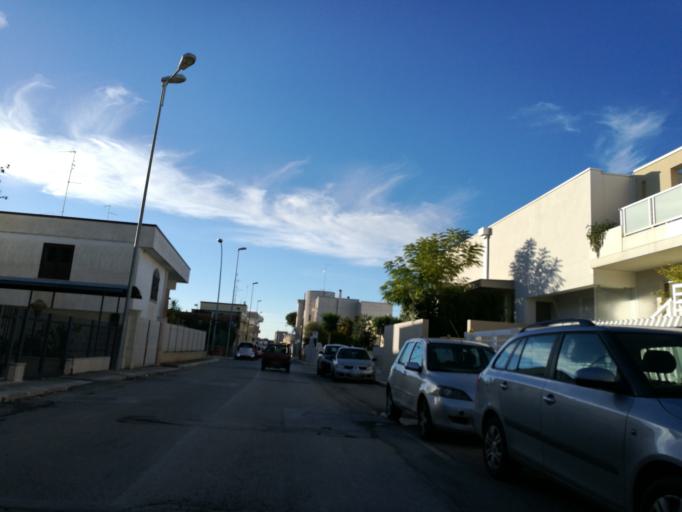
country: IT
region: Apulia
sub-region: Provincia di Bari
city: Adelfia
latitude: 41.0065
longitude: 16.8677
